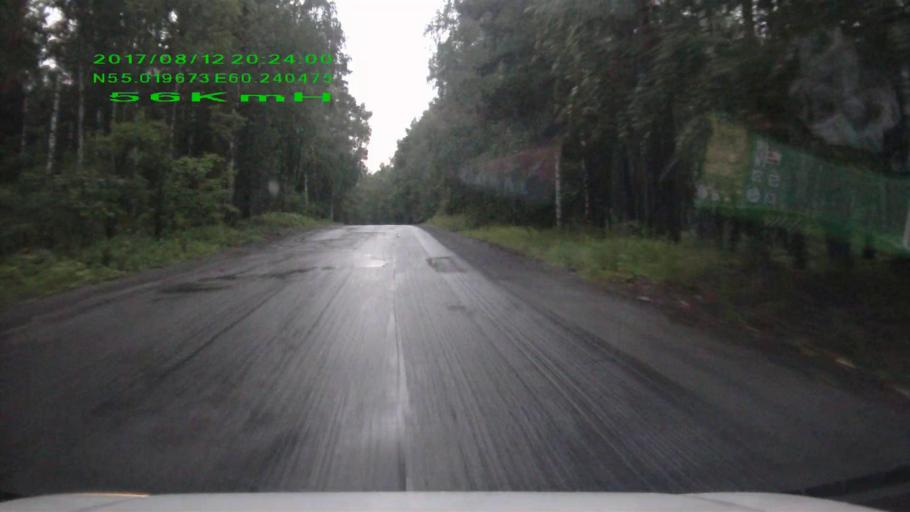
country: RU
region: Chelyabinsk
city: Chebarkul'
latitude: 55.0196
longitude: 60.2399
